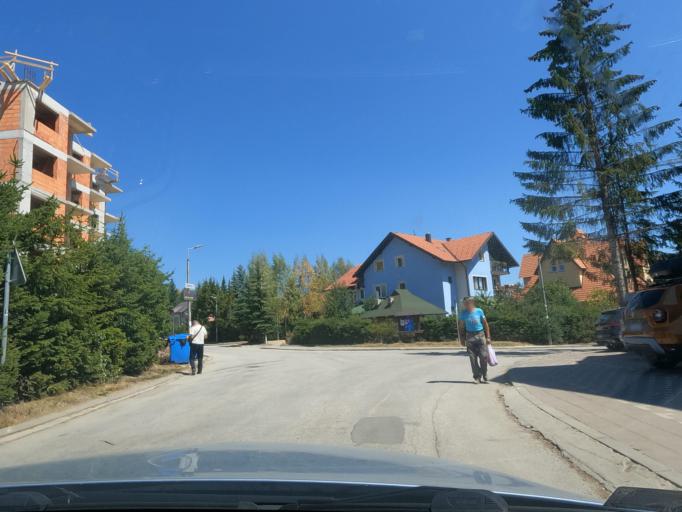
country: RS
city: Zlatibor
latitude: 43.7312
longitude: 19.6941
